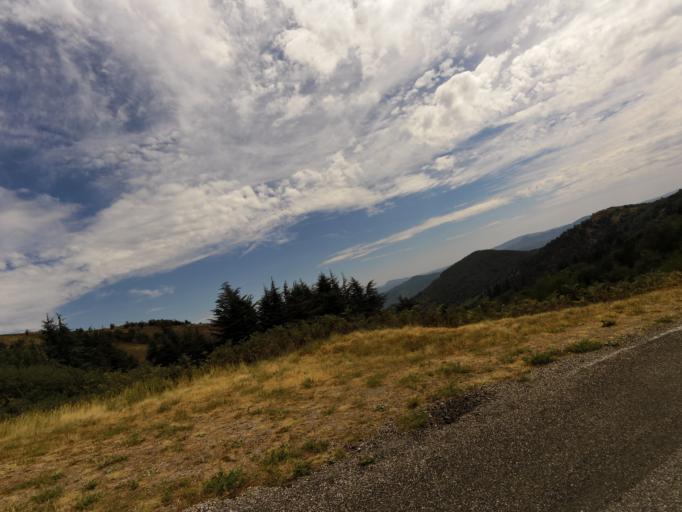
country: FR
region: Languedoc-Roussillon
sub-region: Departement du Gard
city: Valleraugue
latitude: 44.0402
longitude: 3.6071
